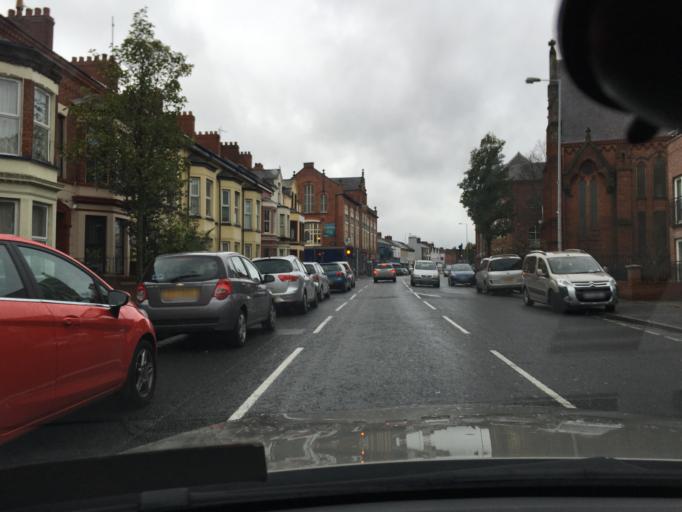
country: GB
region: Northern Ireland
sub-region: Castlereagh District
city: Castlereagh
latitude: 54.5958
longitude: -5.9004
